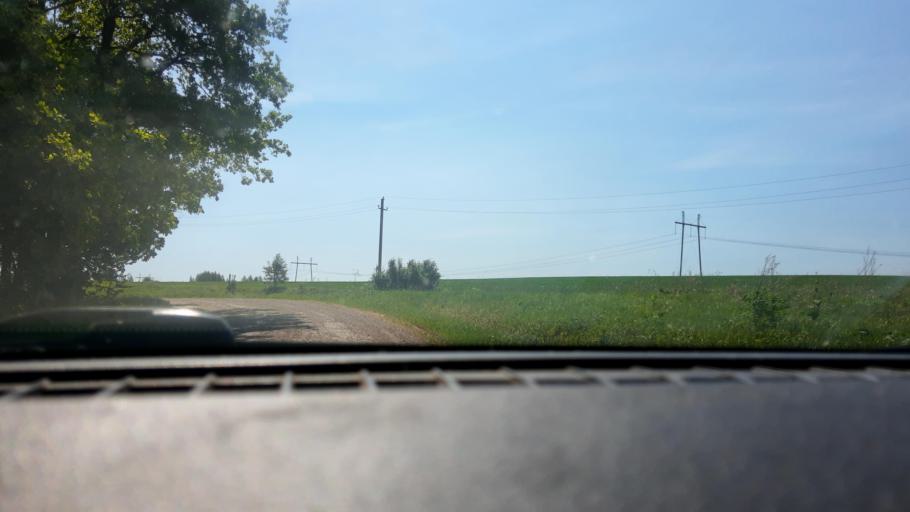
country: RU
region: Bashkortostan
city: Avdon
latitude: 54.4274
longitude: 55.8416
